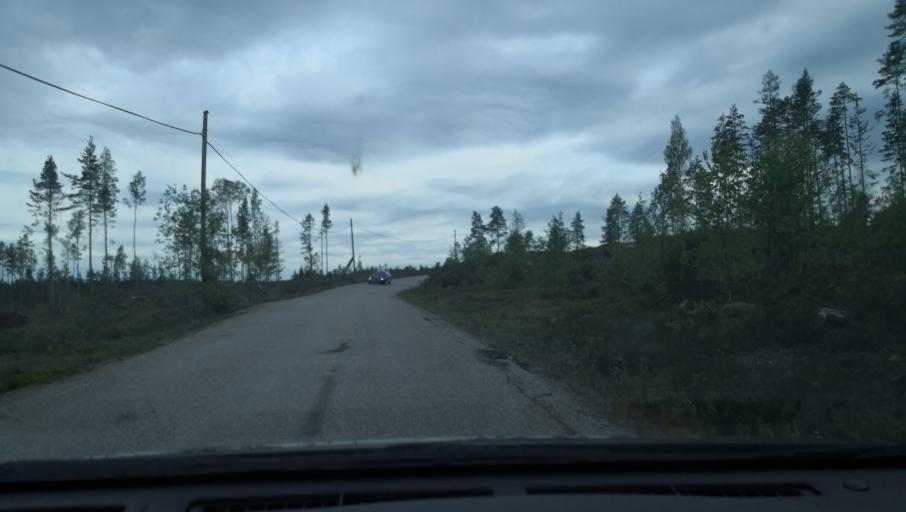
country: SE
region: Vaestmanland
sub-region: Skinnskattebergs Kommun
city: Skinnskatteberg
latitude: 59.8231
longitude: 15.5510
